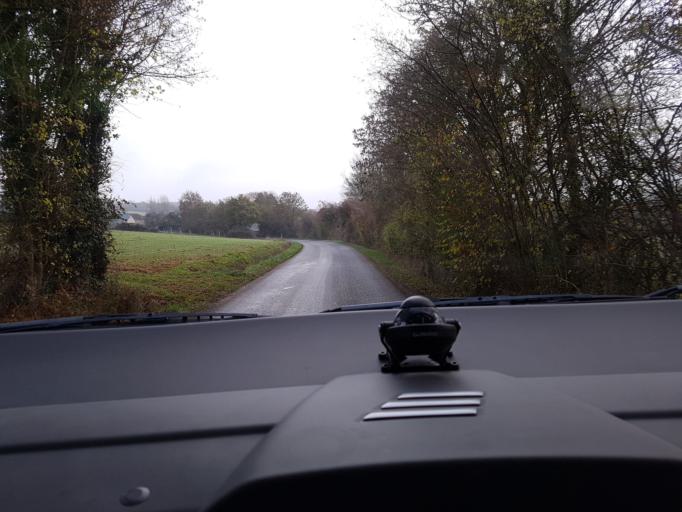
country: FR
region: Lower Normandy
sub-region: Departement de l'Orne
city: Ecouche
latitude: 48.6362
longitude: -0.0478
